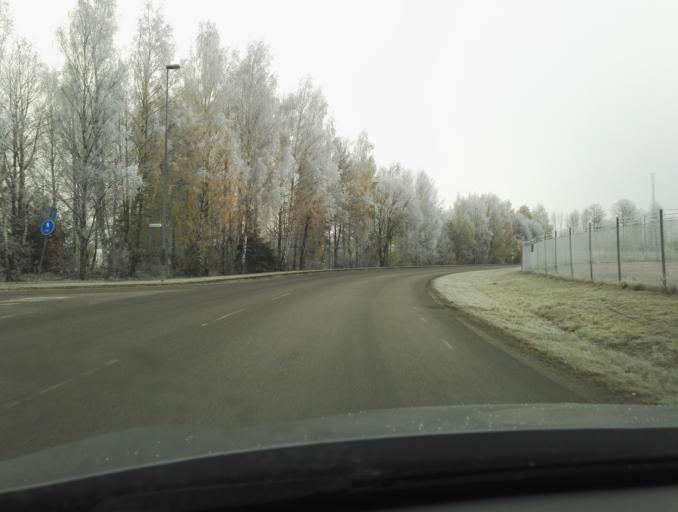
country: SE
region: Kronoberg
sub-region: Vaxjo Kommun
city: Vaexjoe
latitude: 56.8855
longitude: 14.7358
